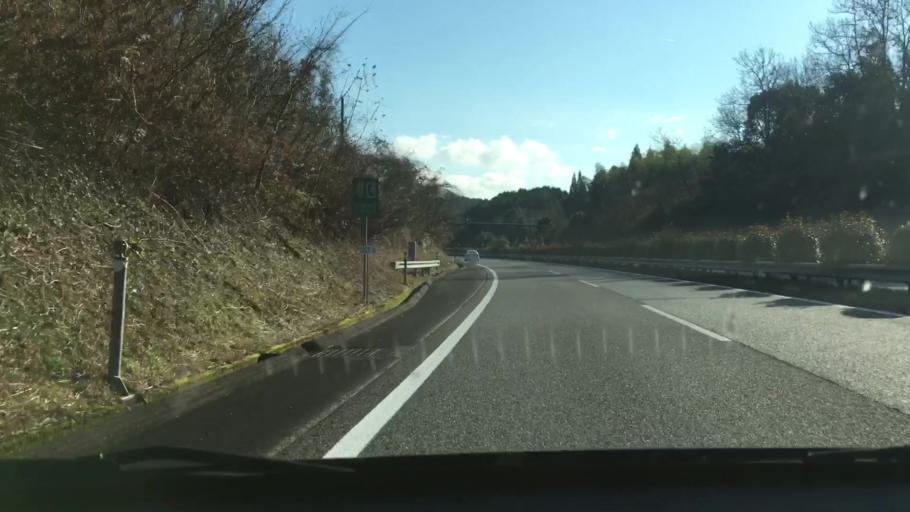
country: JP
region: Kumamoto
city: Hitoyoshi
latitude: 32.1894
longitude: 130.7768
